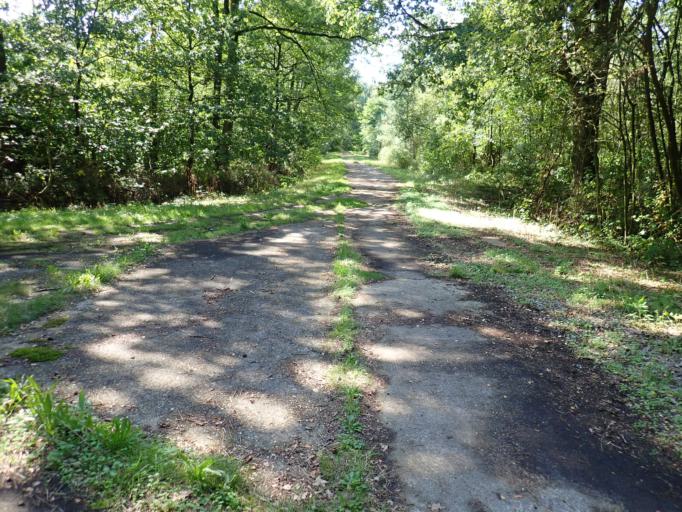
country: BE
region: Flanders
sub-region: Provincie Antwerpen
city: Westerlo
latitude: 51.1226
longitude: 4.9027
